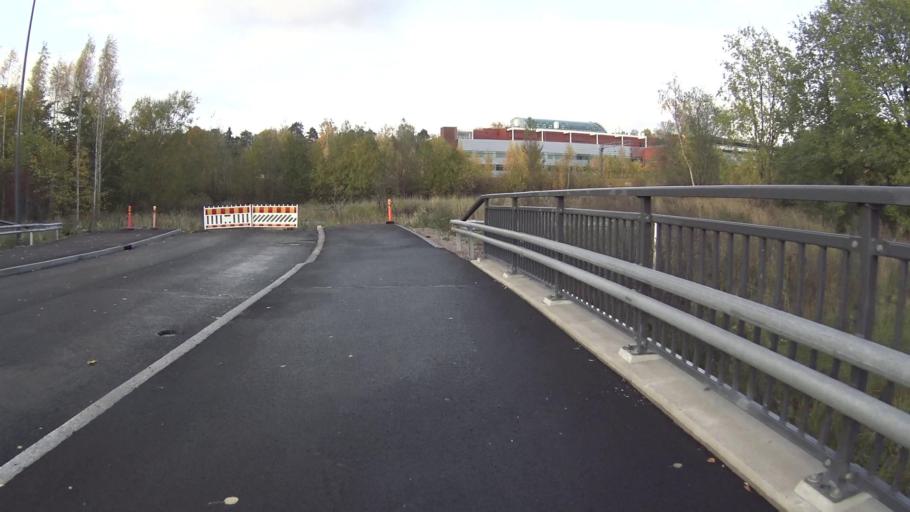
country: FI
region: Uusimaa
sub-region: Helsinki
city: Teekkarikylae
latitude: 60.2176
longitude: 24.8270
